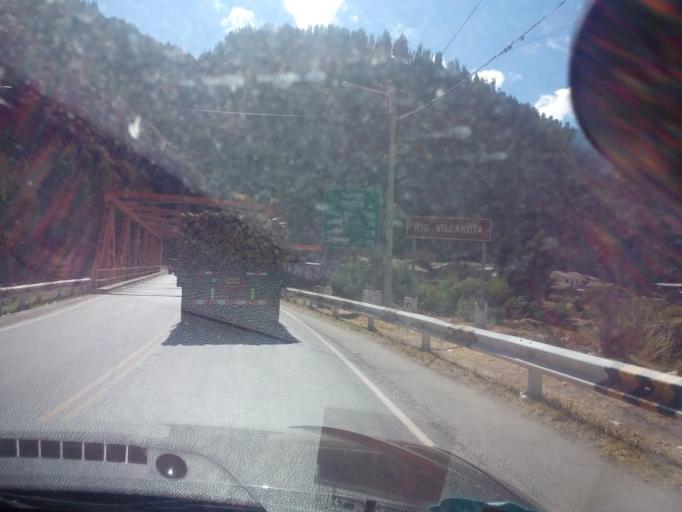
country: PE
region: Cusco
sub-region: Provincia de Quispicanchis
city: Urcos
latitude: -13.6840
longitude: -71.6202
